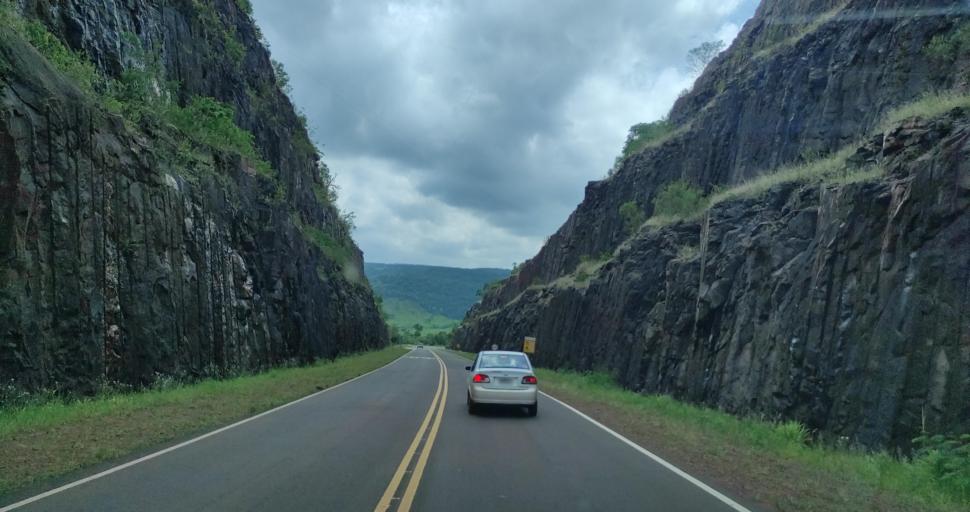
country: AR
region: Misiones
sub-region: Departamento de Veinticinco de Mayo
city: Veinticinco de Mayo
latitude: -27.3766
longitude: -54.8368
